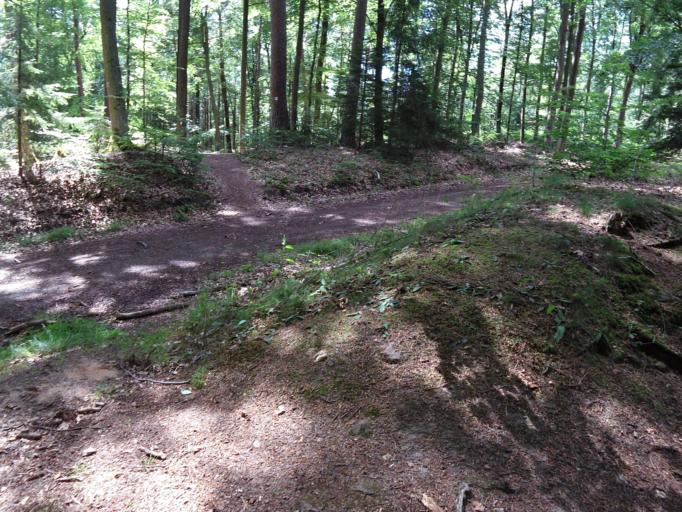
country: DE
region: Rheinland-Pfalz
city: Altleiningen
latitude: 49.4704
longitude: 8.0639
